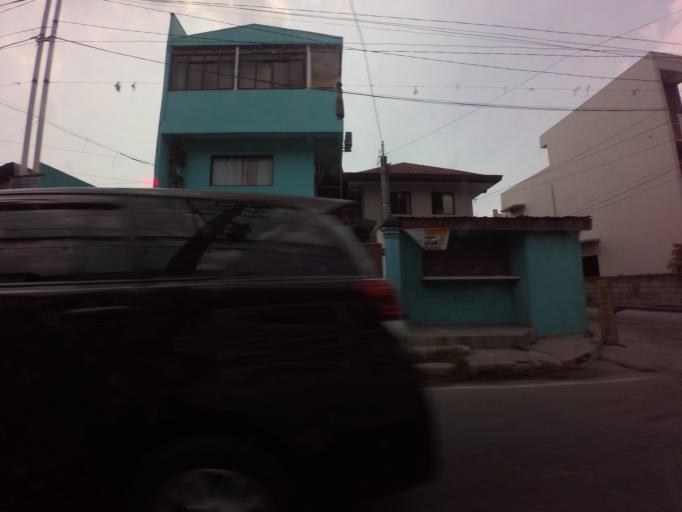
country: PH
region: Calabarzon
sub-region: Province of Rizal
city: Taguig
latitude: 14.4773
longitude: 121.0605
